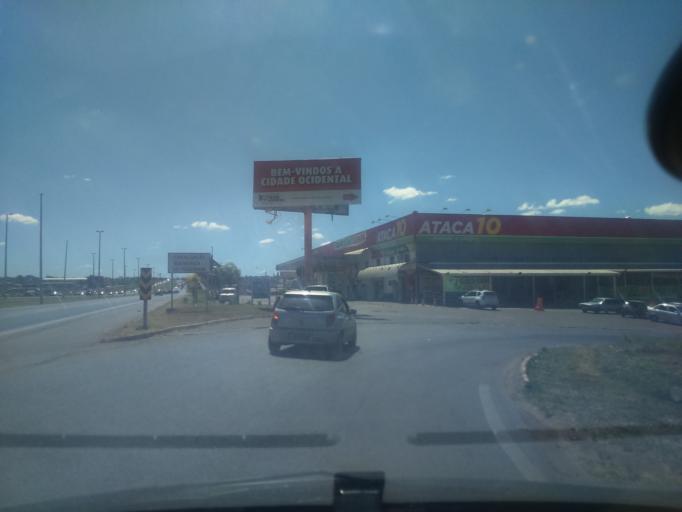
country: BR
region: Goias
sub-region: Luziania
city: Luziania
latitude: -16.1117
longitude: -47.9701
